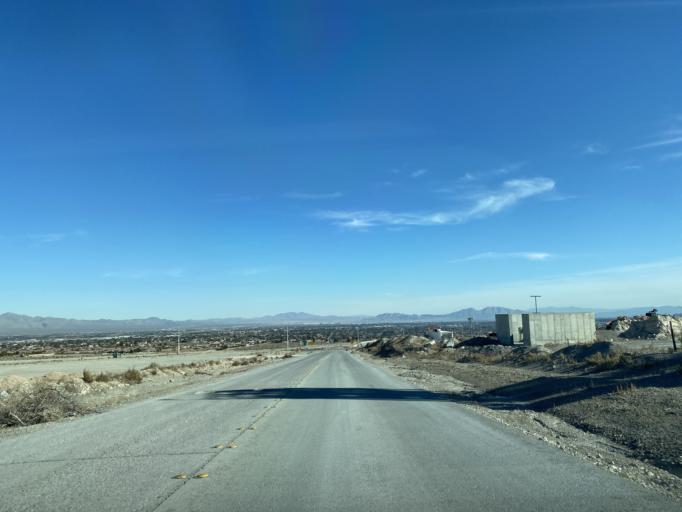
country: US
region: Nevada
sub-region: Clark County
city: Summerlin South
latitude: 36.2552
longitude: -115.3224
